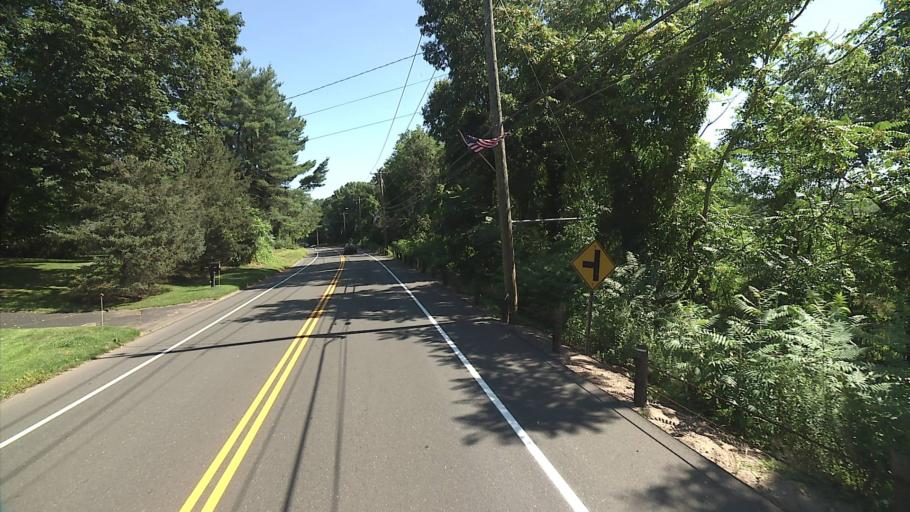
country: US
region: Connecticut
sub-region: Hartford County
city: Simsbury Center
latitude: 41.8919
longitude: -72.7894
